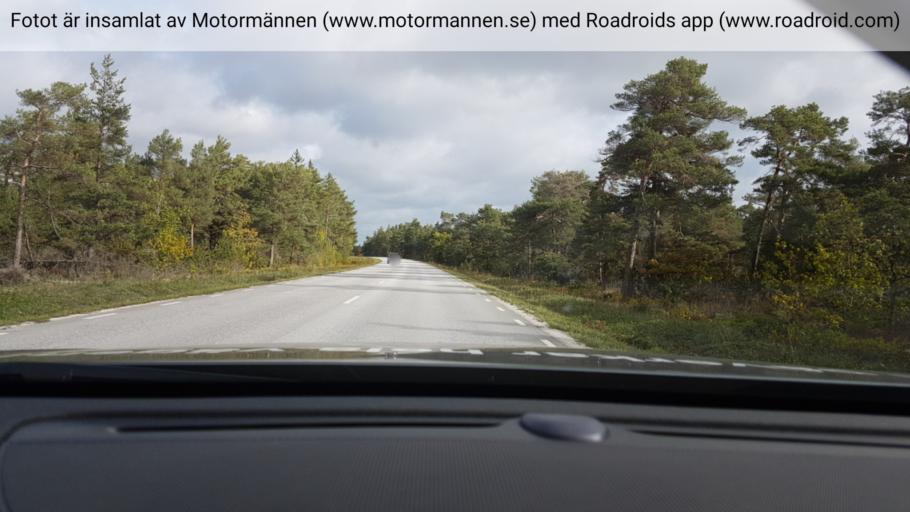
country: SE
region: Gotland
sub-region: Gotland
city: Slite
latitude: 57.7598
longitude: 18.7614
